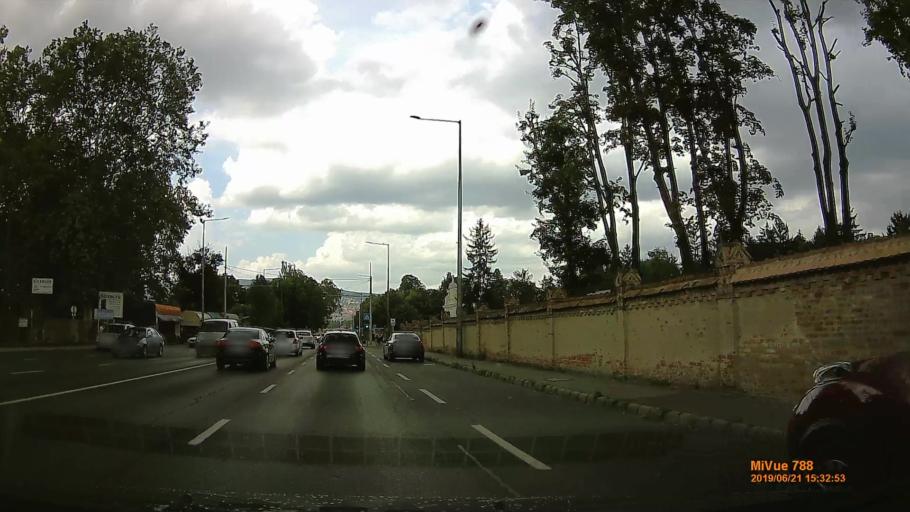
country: HU
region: Baranya
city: Pecs
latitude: 46.0522
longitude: 18.2313
